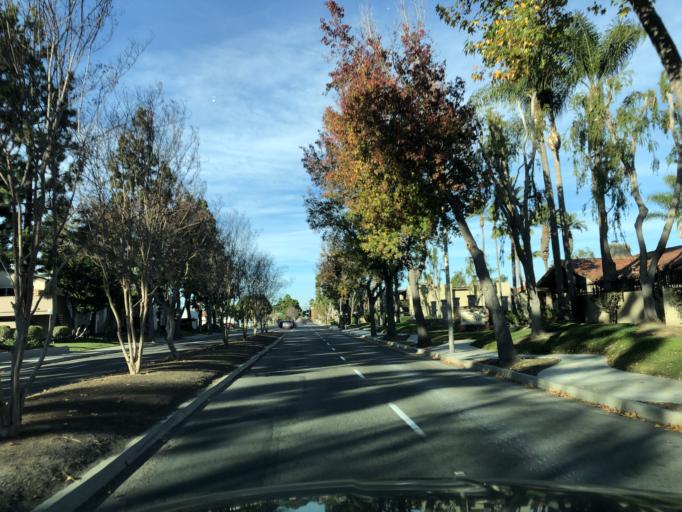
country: US
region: California
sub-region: Orange County
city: Tustin
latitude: 33.7567
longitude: -117.8416
